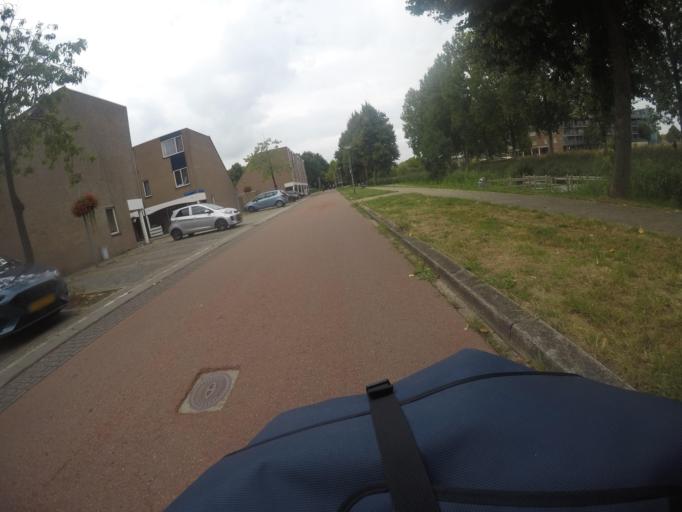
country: NL
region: Flevoland
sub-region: Gemeente Almere
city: Almere Stad
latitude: 52.3765
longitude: 5.2102
